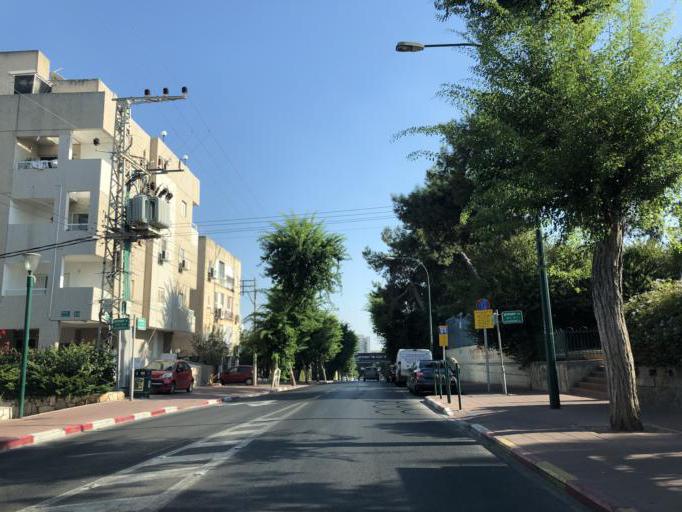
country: IL
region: Tel Aviv
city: Giv`atayim
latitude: 32.0681
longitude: 34.8243
